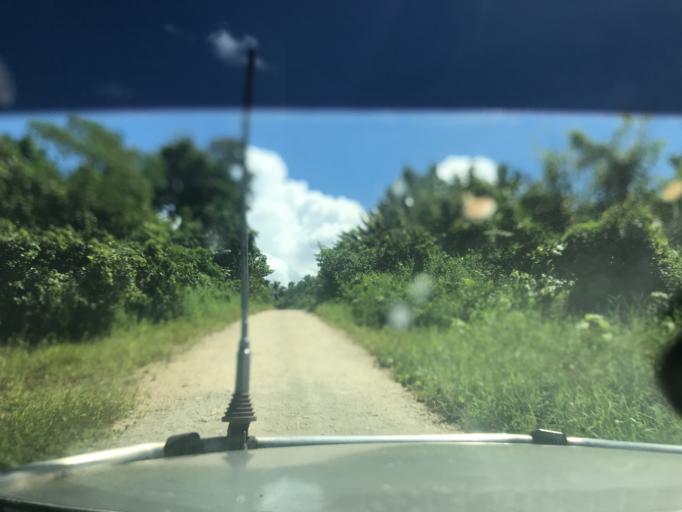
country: SB
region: Malaita
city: Auki
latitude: -8.7286
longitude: 160.9077
